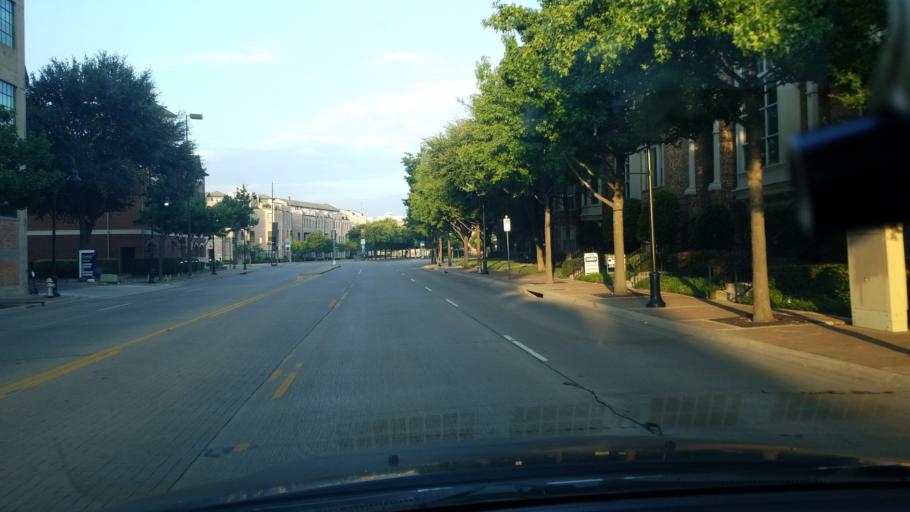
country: US
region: Texas
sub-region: Dallas County
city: Dallas
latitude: 32.7809
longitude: -96.7886
